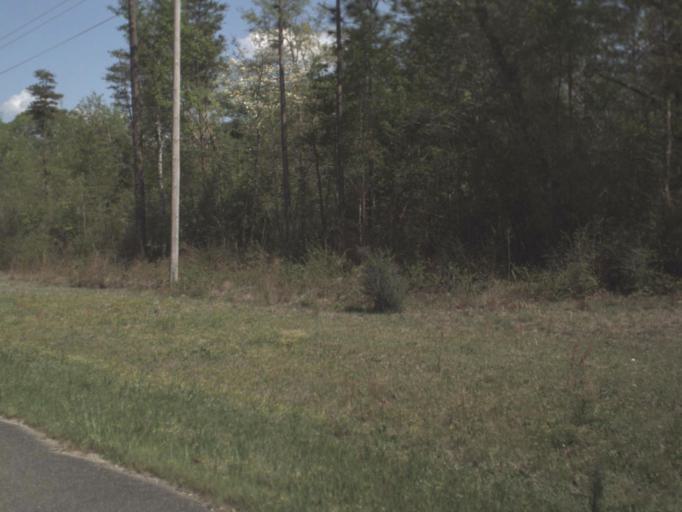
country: US
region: Alabama
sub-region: Escambia County
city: East Brewton
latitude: 30.9161
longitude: -87.0436
